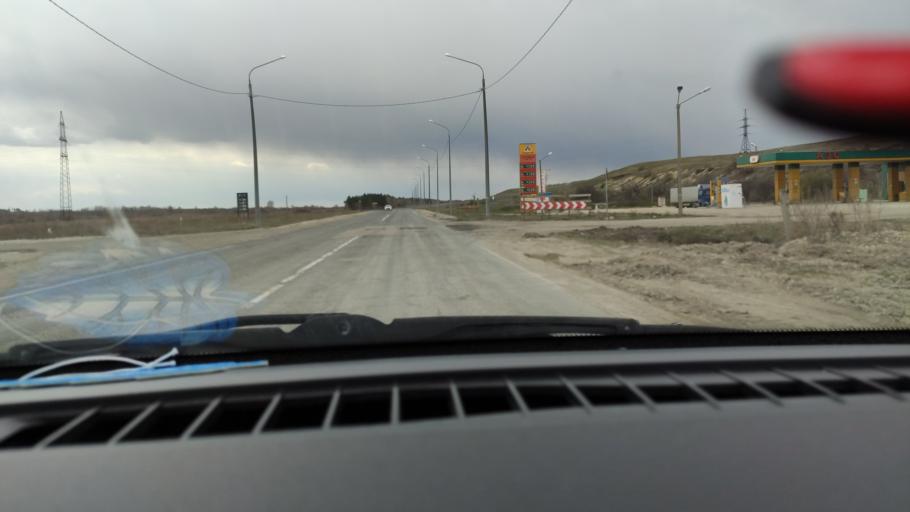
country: RU
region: Saratov
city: Sinodskoye
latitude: 52.0791
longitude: 46.7929
